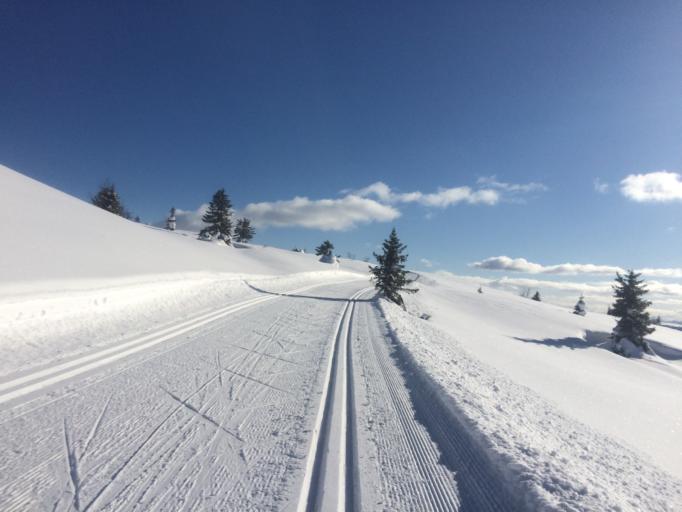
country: NO
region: Oppland
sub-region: Ringebu
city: Ringebu
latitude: 61.3738
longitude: 10.0600
